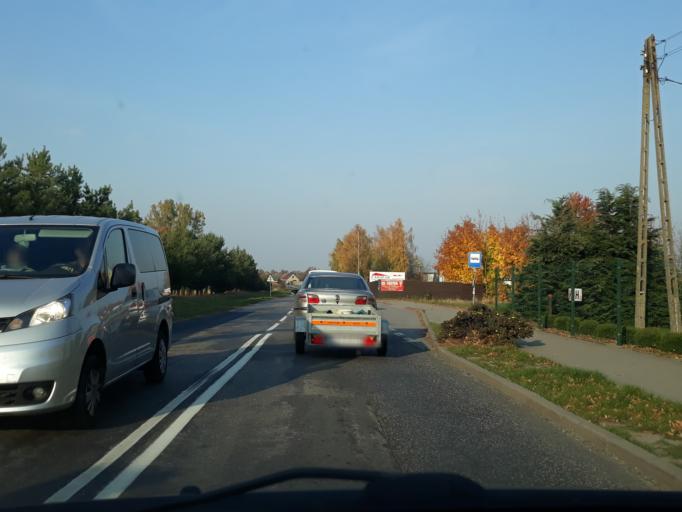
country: PL
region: Pomeranian Voivodeship
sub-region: Powiat chojnicki
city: Chojnice
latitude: 53.6672
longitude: 17.5303
